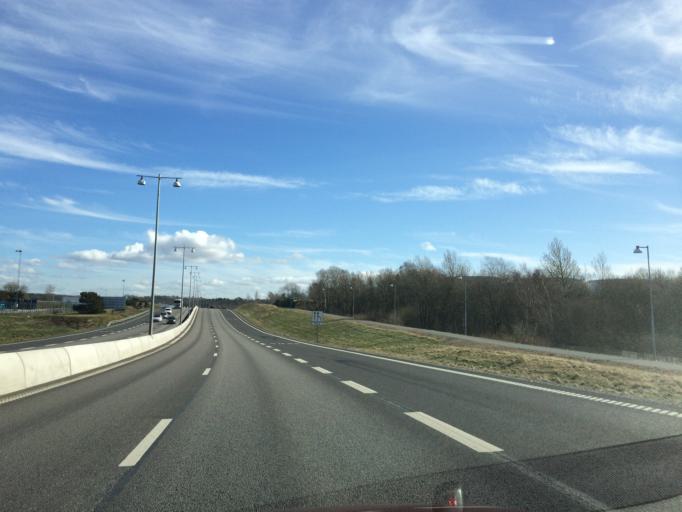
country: SE
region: Vaestra Goetaland
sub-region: Goteborg
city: Torslanda
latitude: 57.7157
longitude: 11.8274
